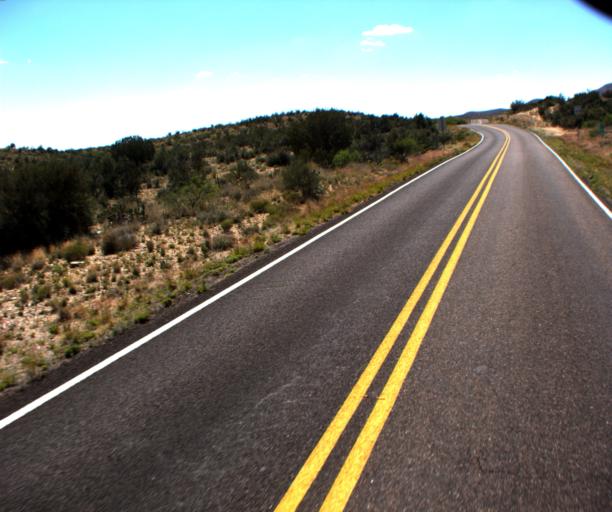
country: US
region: Arizona
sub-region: Yavapai County
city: Bagdad
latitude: 34.5184
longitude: -113.1390
